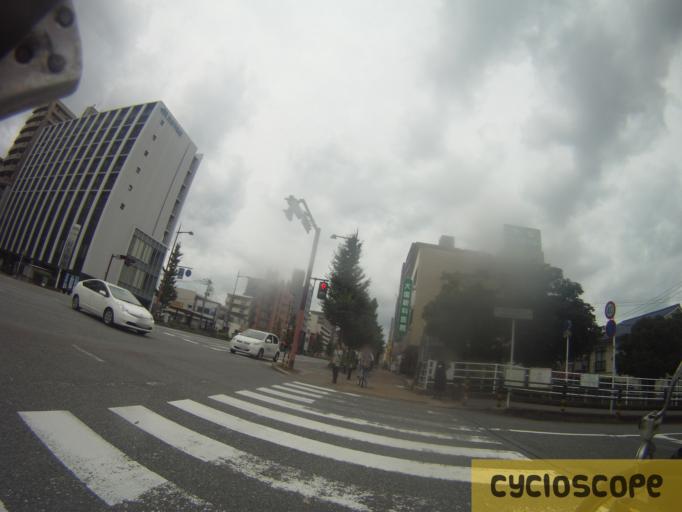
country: JP
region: Fukuoka
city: Fukuoka-shi
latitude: 33.5888
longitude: 130.3672
